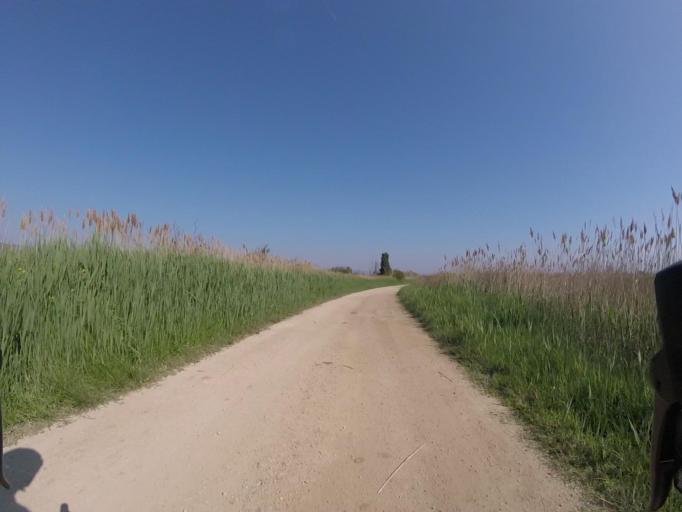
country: ES
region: Valencia
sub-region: Provincia de Castello
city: Orpesa/Oropesa del Mar
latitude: 40.1422
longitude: 0.1639
